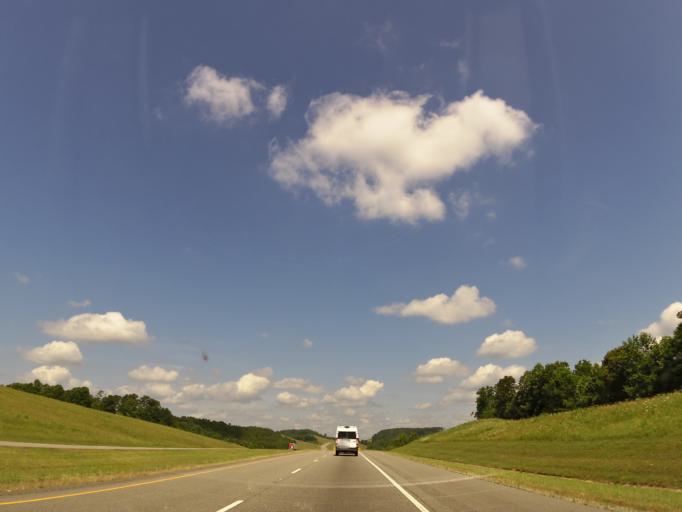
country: US
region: Alabama
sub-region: Marion County
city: Winfield
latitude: 34.0002
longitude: -87.8096
